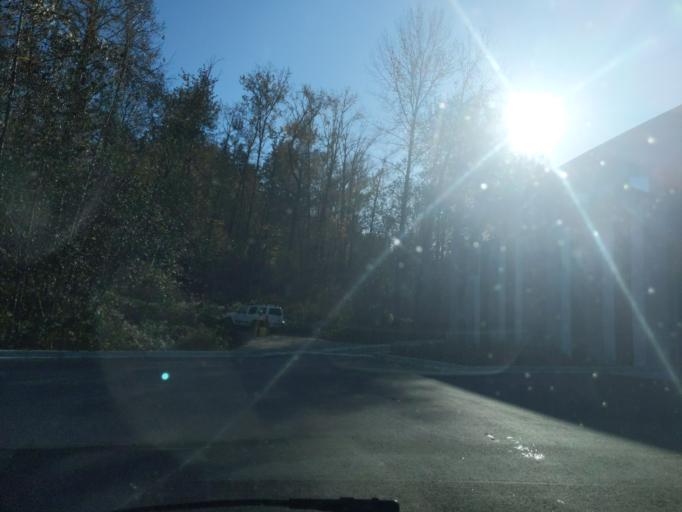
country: CA
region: British Columbia
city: New Westminster
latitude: 49.2016
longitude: -122.8697
